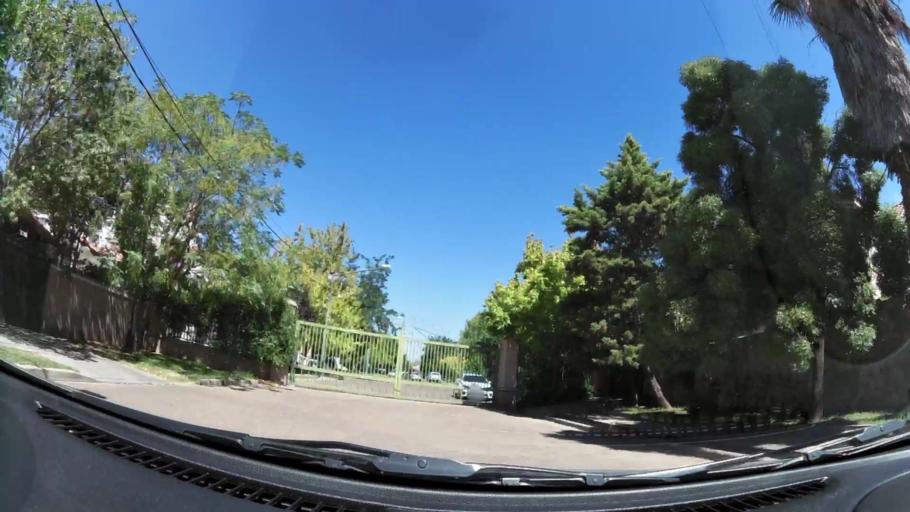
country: AR
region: Mendoza
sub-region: Departamento de Godoy Cruz
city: Godoy Cruz
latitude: -32.9513
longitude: -68.8599
